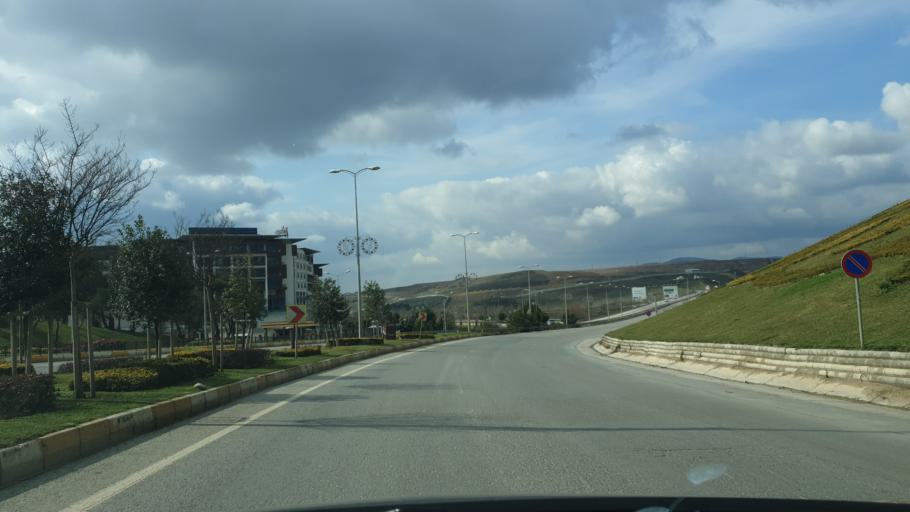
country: TR
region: Istanbul
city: Icmeler
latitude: 40.8762
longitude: 29.3192
